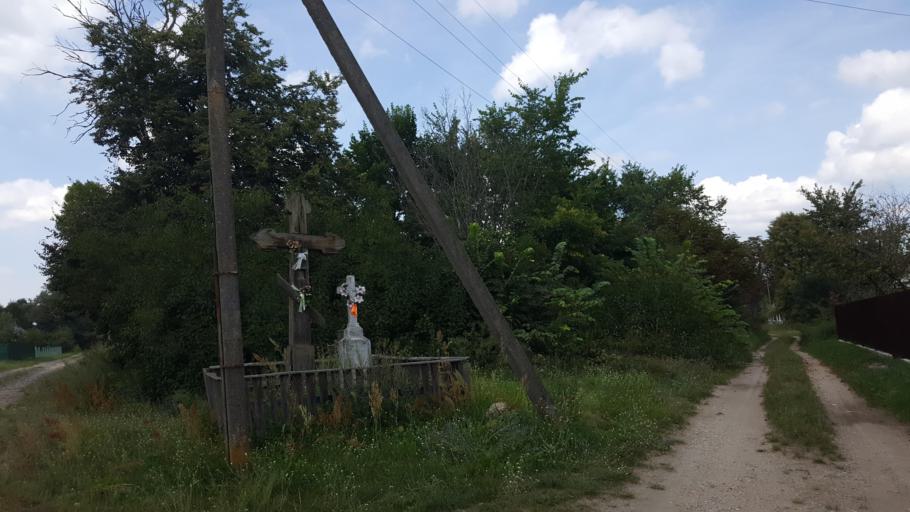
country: PL
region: Podlasie
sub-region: Powiat hajnowski
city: Hajnowka
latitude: 52.5663
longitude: 23.6088
